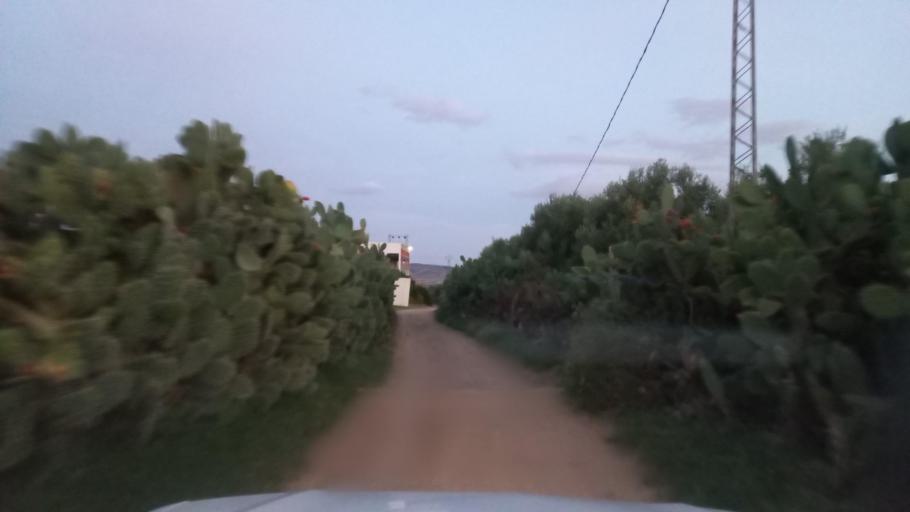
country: TN
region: Al Qasrayn
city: Sbiba
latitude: 35.4164
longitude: 9.1199
